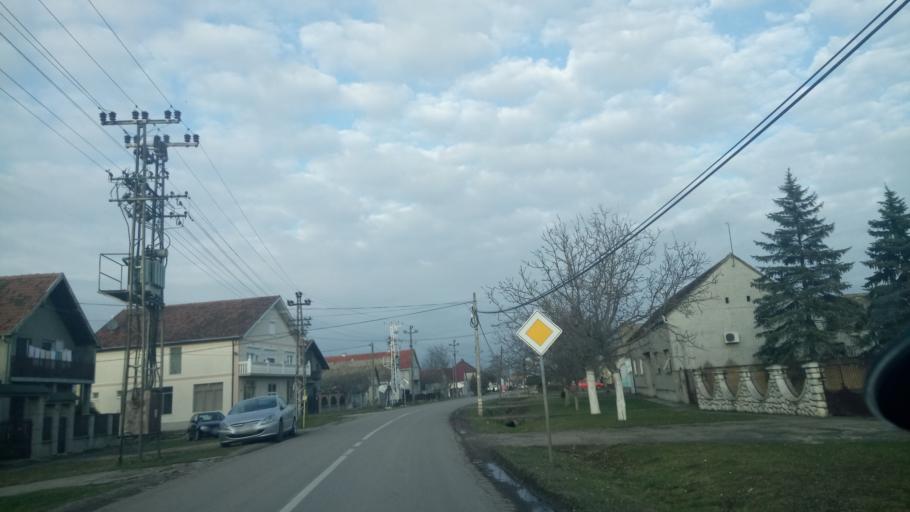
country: RS
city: Vojka
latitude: 44.9361
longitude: 20.1659
